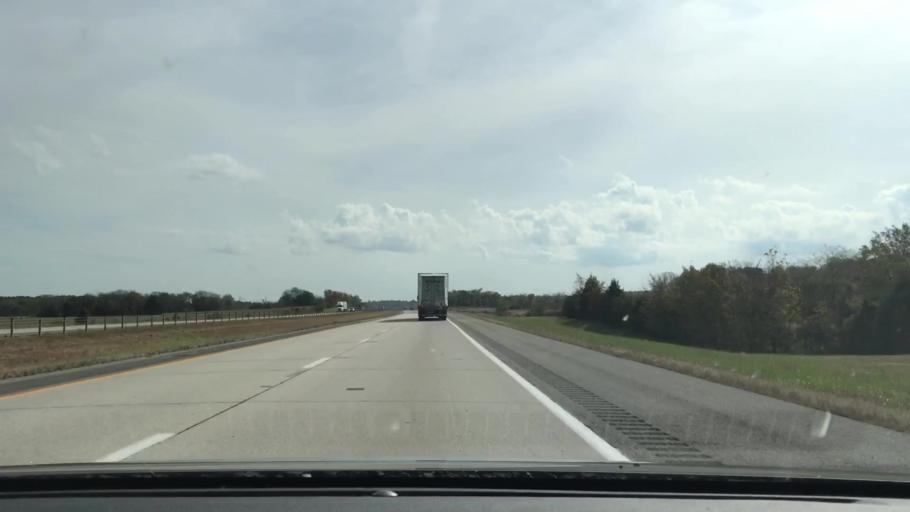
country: US
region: Kentucky
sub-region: Trigg County
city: Cadiz
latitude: 36.9197
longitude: -87.7968
